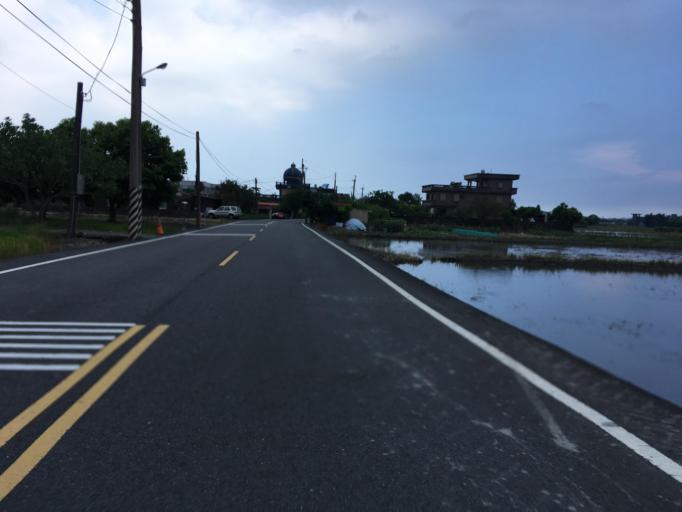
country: TW
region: Taiwan
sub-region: Yilan
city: Yilan
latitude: 24.6839
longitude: 121.7017
